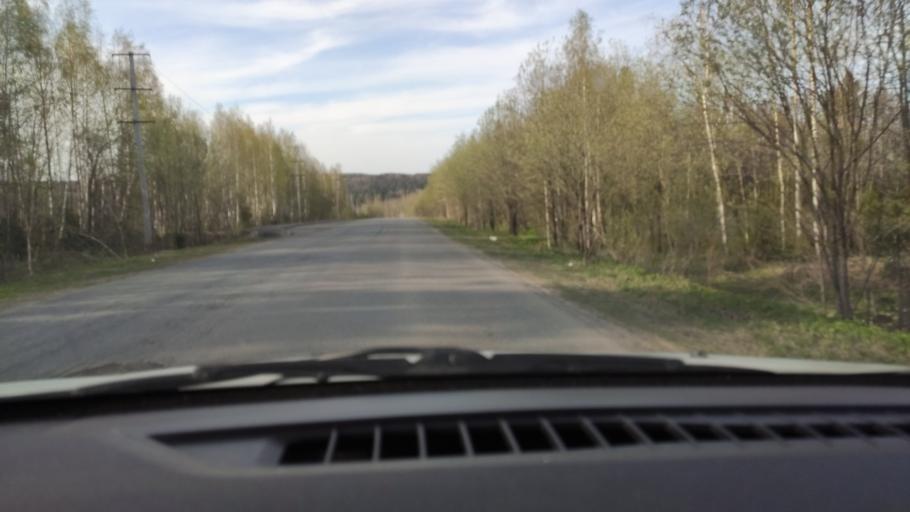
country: RU
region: Perm
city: Novyye Lyady
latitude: 57.9479
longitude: 56.5688
